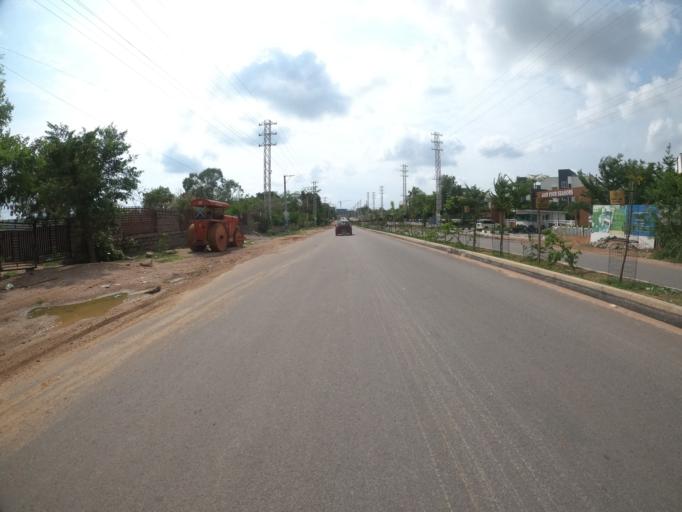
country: IN
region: Telangana
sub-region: Medak
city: Serilingampalle
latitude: 17.3862
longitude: 78.3300
